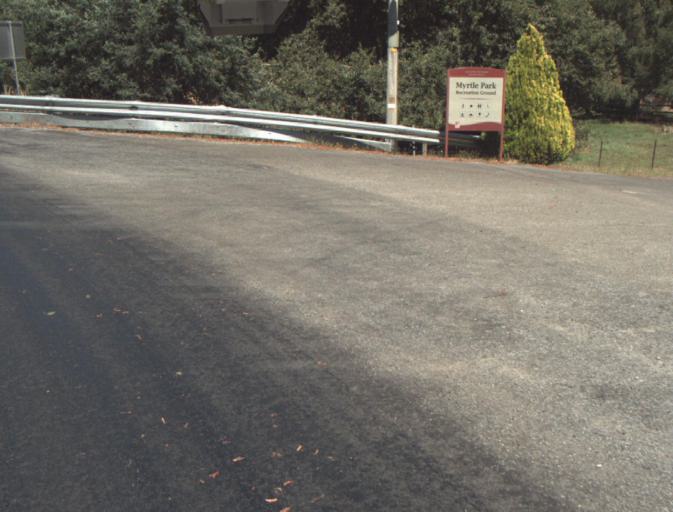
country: AU
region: Tasmania
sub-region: Dorset
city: Scottsdale
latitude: -41.3108
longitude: 147.3675
